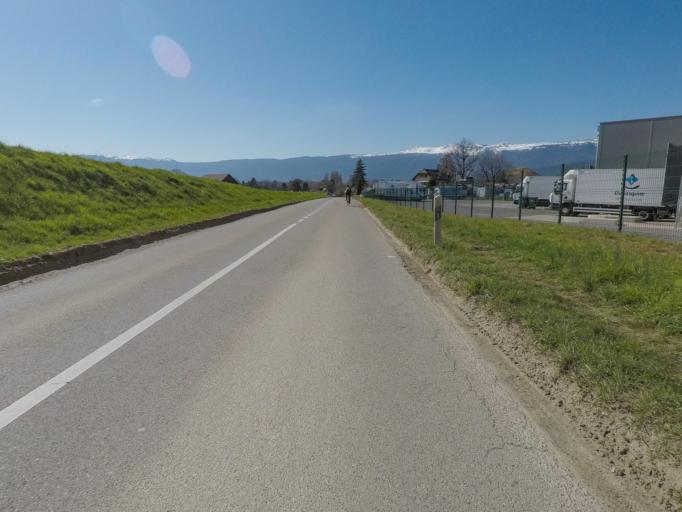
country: CH
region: Geneva
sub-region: Geneva
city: Vernier
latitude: 46.2165
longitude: 6.0726
